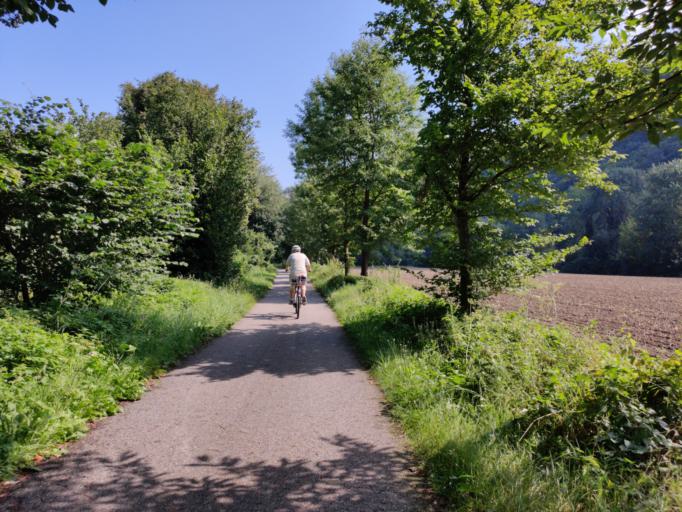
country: AT
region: Lower Austria
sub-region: Politischer Bezirk Krems
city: Aggsbach
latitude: 48.2812
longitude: 15.4009
